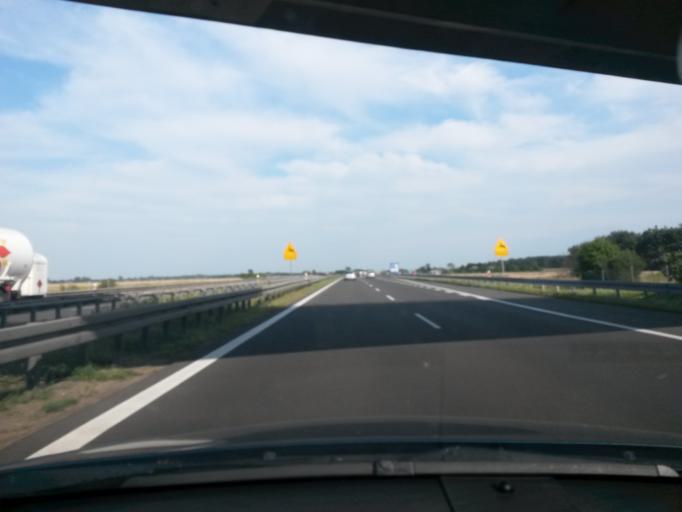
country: PL
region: Greater Poland Voivodeship
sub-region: Powiat slupecki
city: Ladek
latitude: 52.2282
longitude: 17.9231
